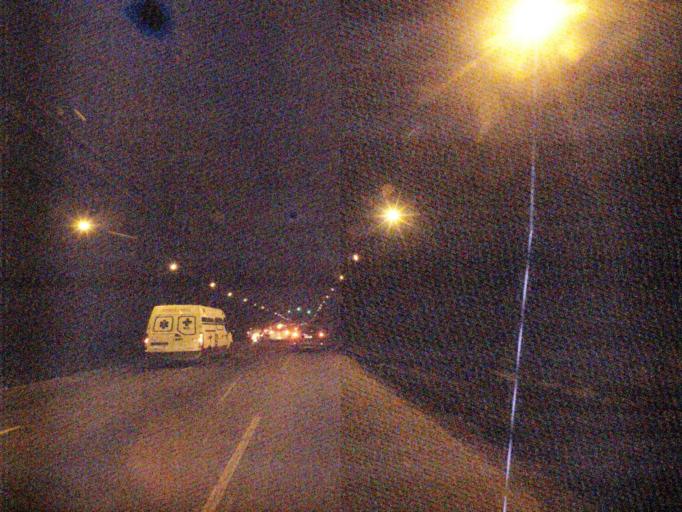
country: BR
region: Rio de Janeiro
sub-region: Rio De Janeiro
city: Rio de Janeiro
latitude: -22.9551
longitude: -43.2036
